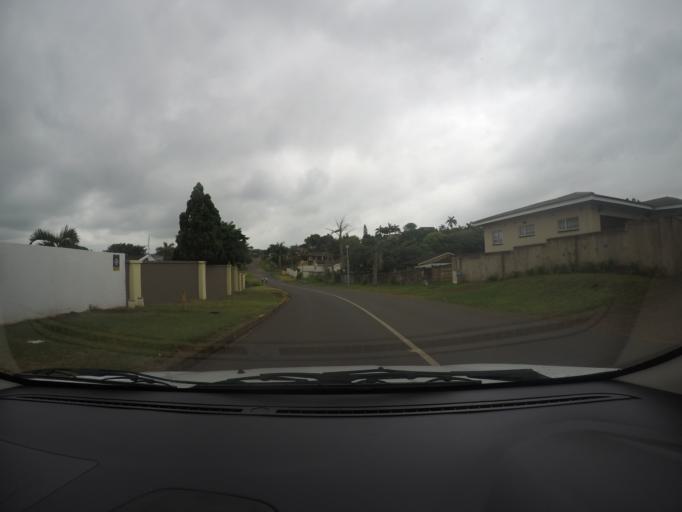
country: ZA
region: KwaZulu-Natal
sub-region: uThungulu District Municipality
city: Empangeni
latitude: -28.7642
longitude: 31.8876
